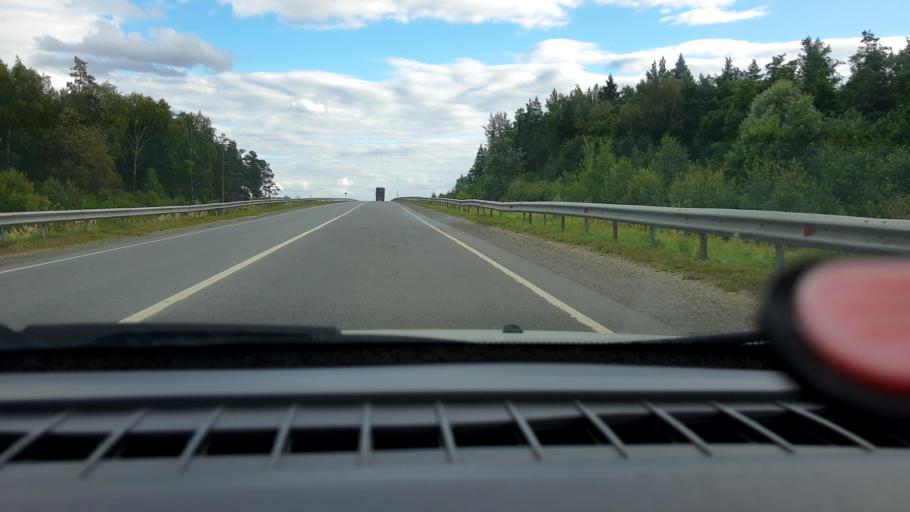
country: RU
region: Nizjnij Novgorod
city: Kstovo
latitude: 56.1572
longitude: 44.1549
